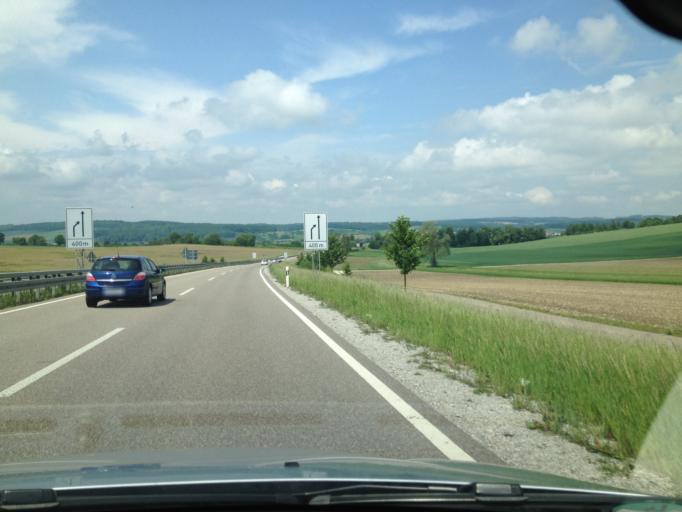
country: DE
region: Bavaria
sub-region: Swabia
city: Donauwoerth
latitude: 48.7398
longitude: 10.7482
